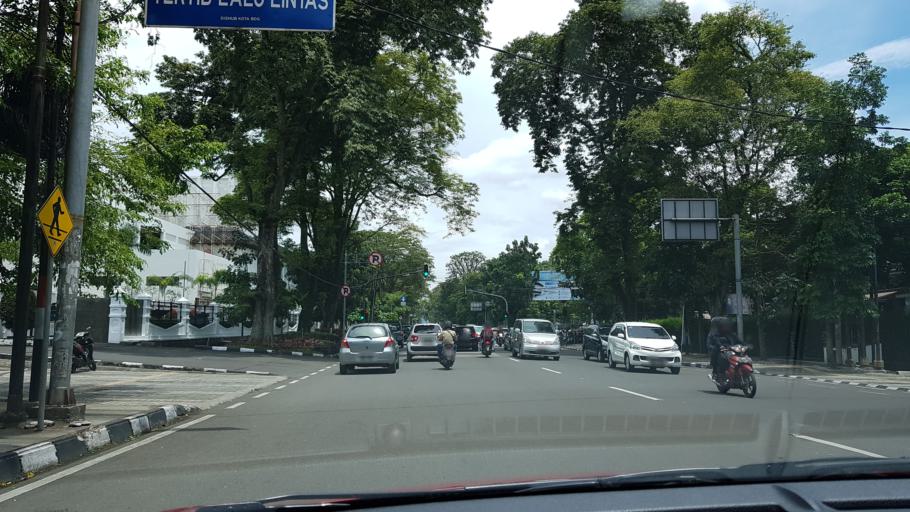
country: ID
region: West Java
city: Bandung
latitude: -6.9014
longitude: 107.6161
